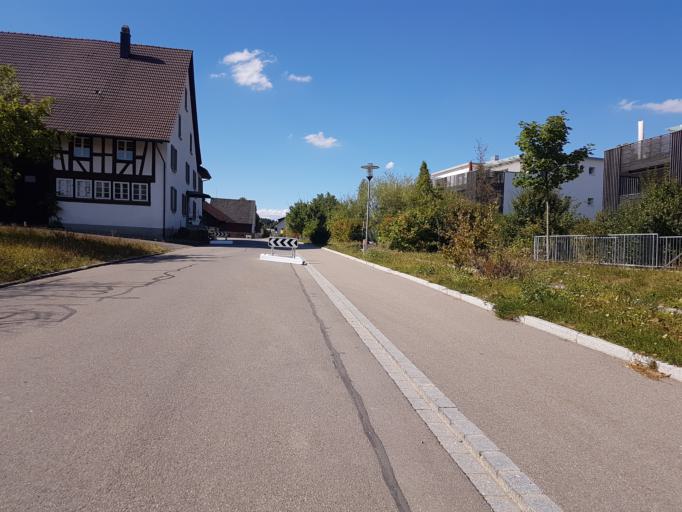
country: CH
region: Zurich
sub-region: Bezirk Pfaeffikon
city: Tagelswangen
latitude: 47.4275
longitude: 8.6741
